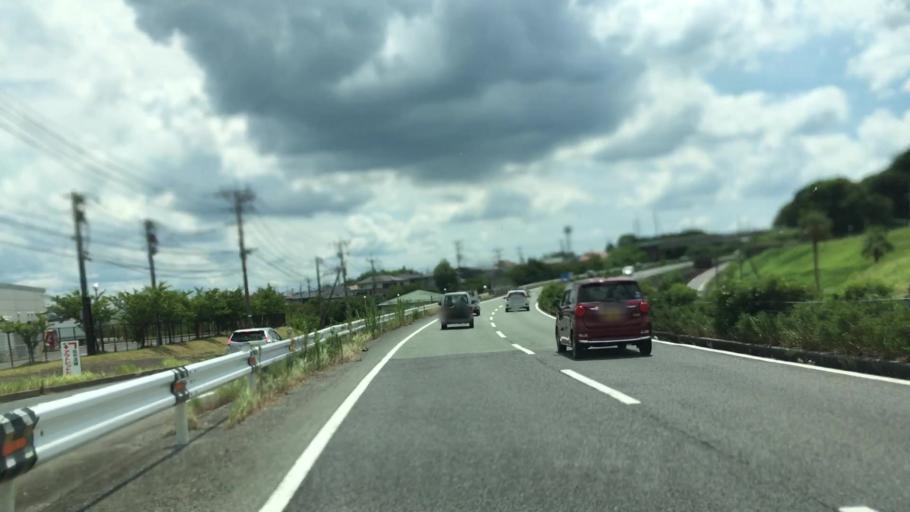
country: JP
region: Saga Prefecture
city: Tosu
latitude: 33.4044
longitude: 130.5136
